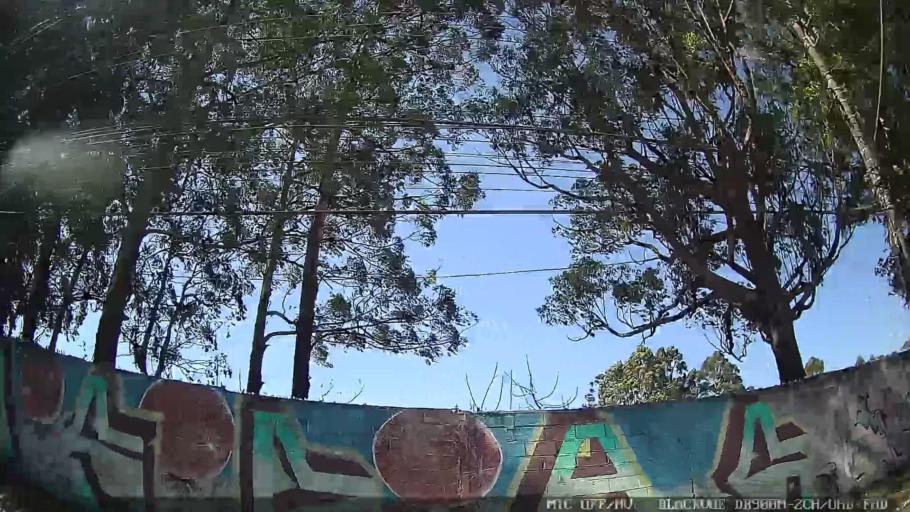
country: BR
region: Sao Paulo
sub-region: Sao Caetano Do Sul
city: Sao Caetano do Sul
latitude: -23.5521
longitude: -46.4742
